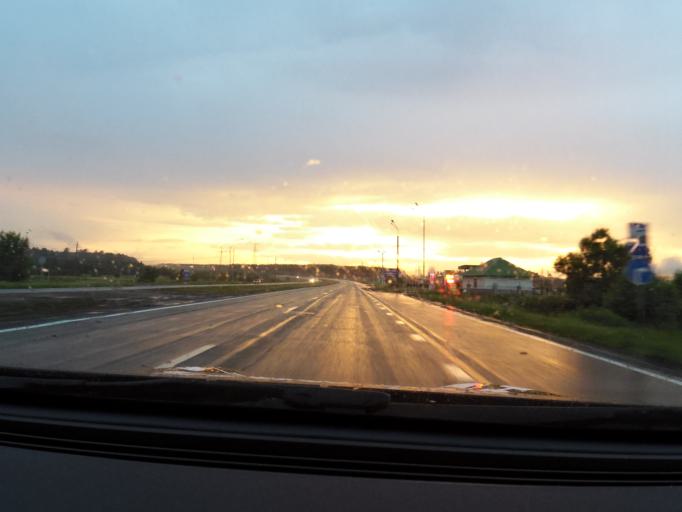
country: RU
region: Tatarstan
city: Yelabuga
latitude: 55.7770
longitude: 52.2026
